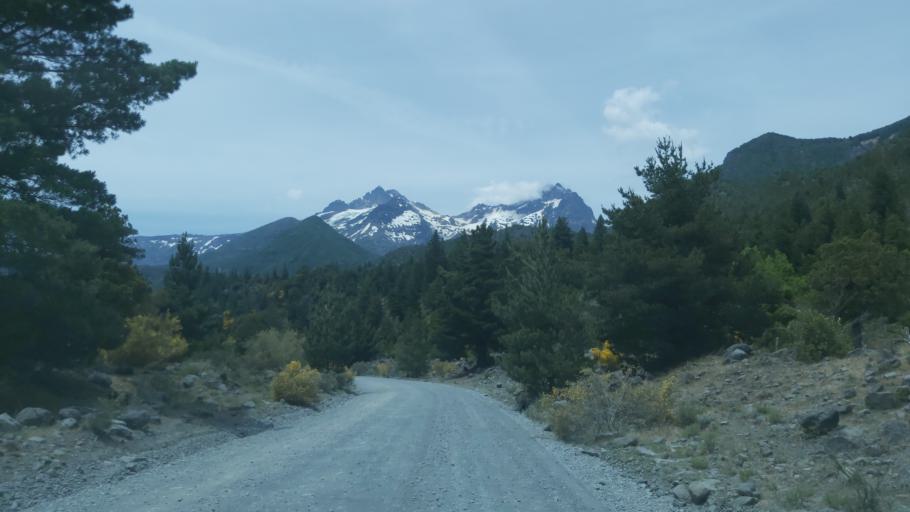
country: AR
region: Neuquen
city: Las Ovejas
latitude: -37.3887
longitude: -71.4681
